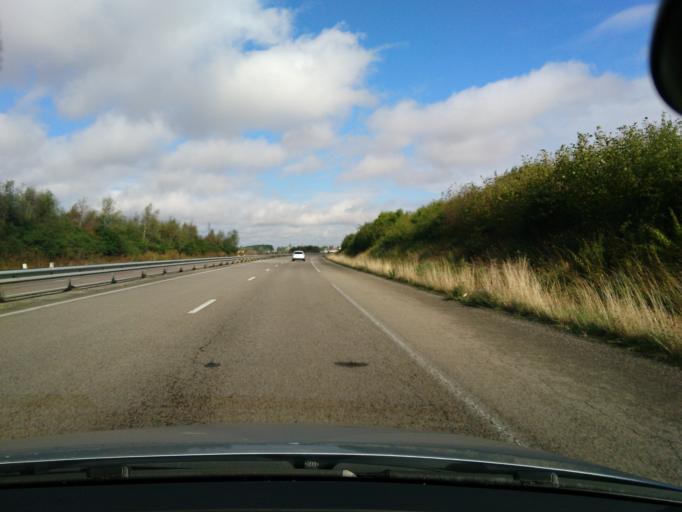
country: FR
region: Haute-Normandie
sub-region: Departement de l'Eure
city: Damville
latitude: 48.8952
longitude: 1.1715
